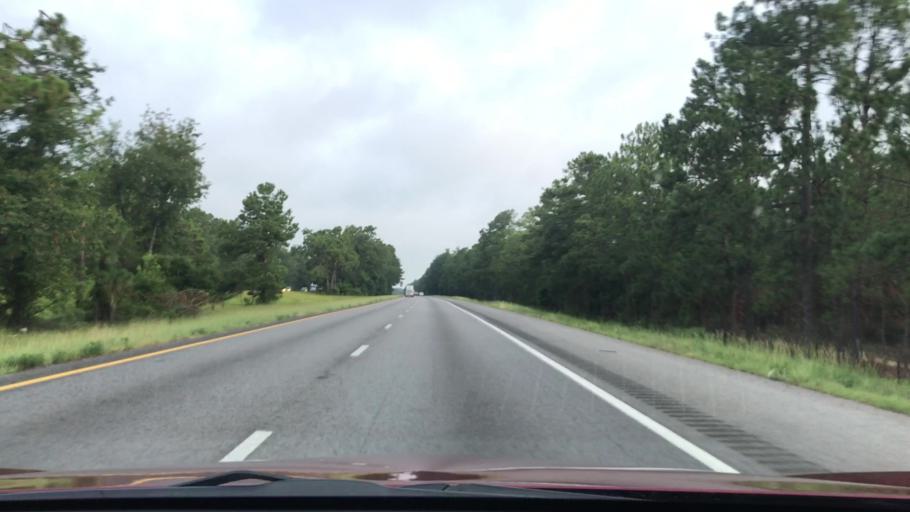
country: US
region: South Carolina
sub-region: Dorchester County
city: Ridgeville
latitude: 33.1714
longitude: -80.3657
